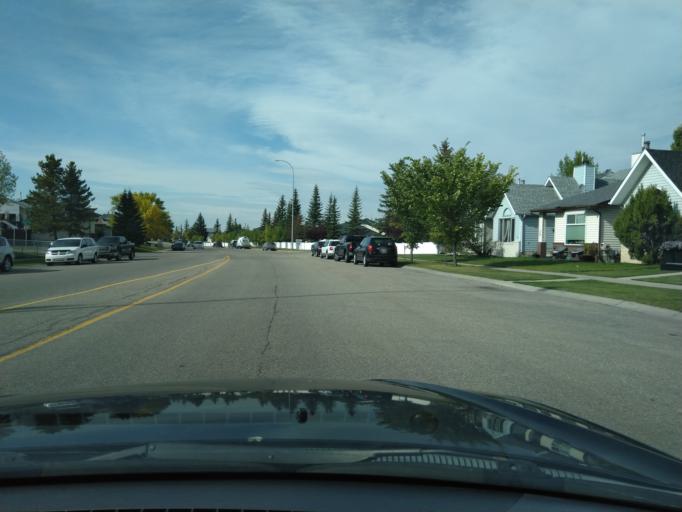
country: CA
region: Alberta
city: Calgary
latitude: 51.1375
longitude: -114.0913
